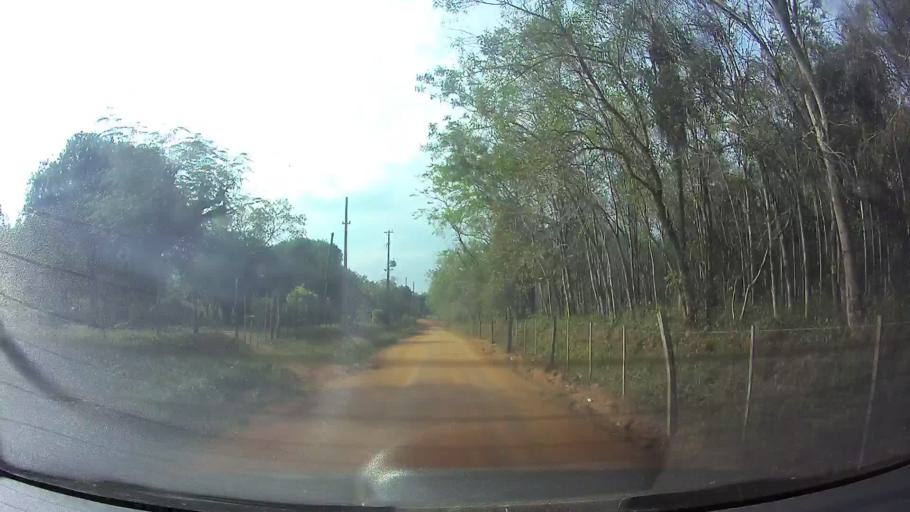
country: PY
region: Cordillera
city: Arroyos y Esteros
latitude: -25.0120
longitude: -57.1984
